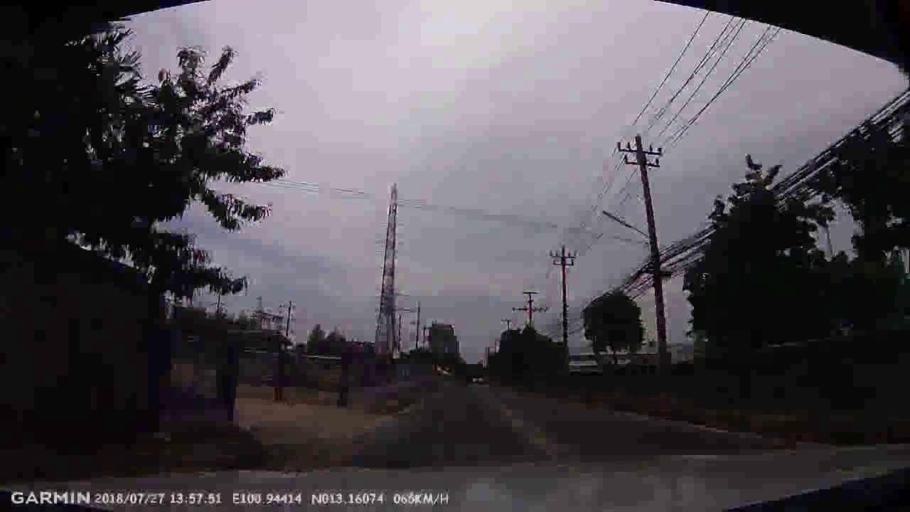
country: TH
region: Chon Buri
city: Si Racha
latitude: 13.1608
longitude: 100.9441
